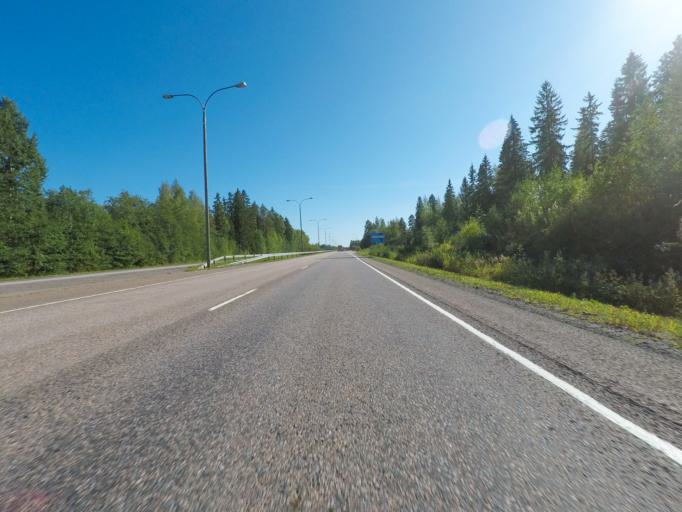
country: FI
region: Northern Savo
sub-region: Varkaus
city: Varkaus
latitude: 62.3106
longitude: 27.8552
